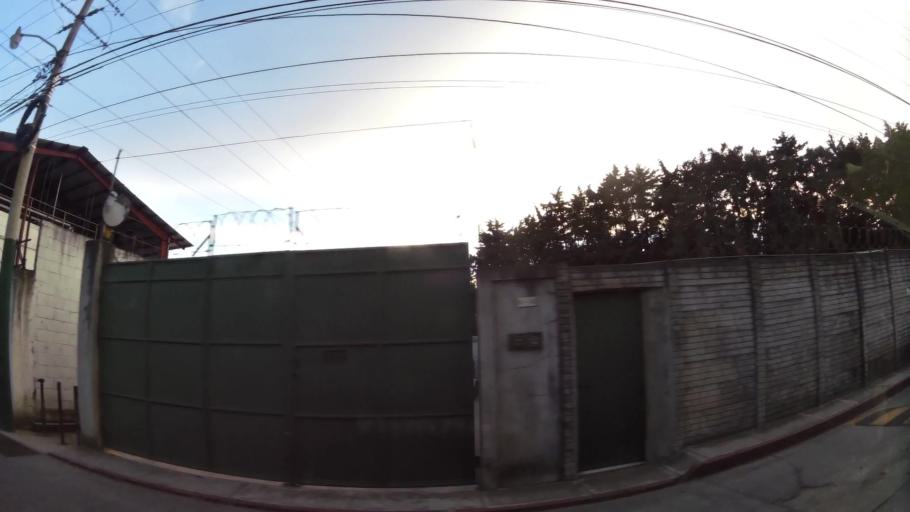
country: GT
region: Sacatepequez
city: San Lucas Sacatepequez
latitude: 14.6097
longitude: -90.6665
